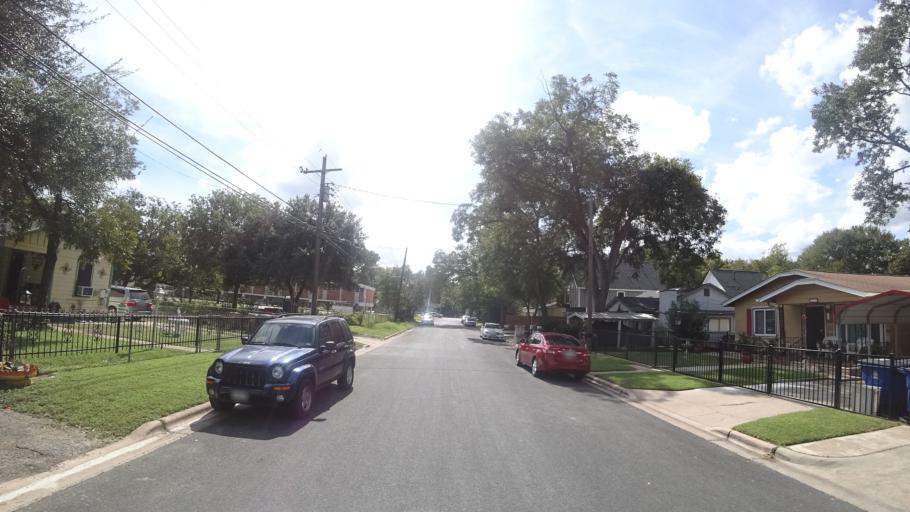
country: US
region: Texas
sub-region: Travis County
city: Austin
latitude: 30.2640
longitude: -97.7055
